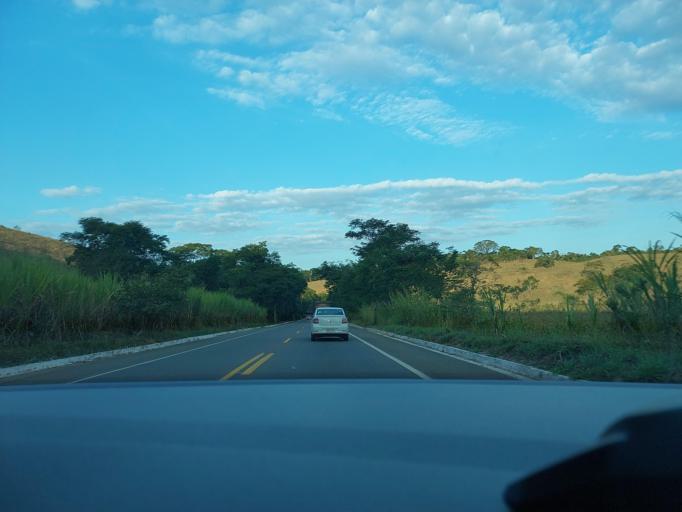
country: BR
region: Minas Gerais
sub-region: Muriae
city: Muriae
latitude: -21.1221
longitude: -42.2203
